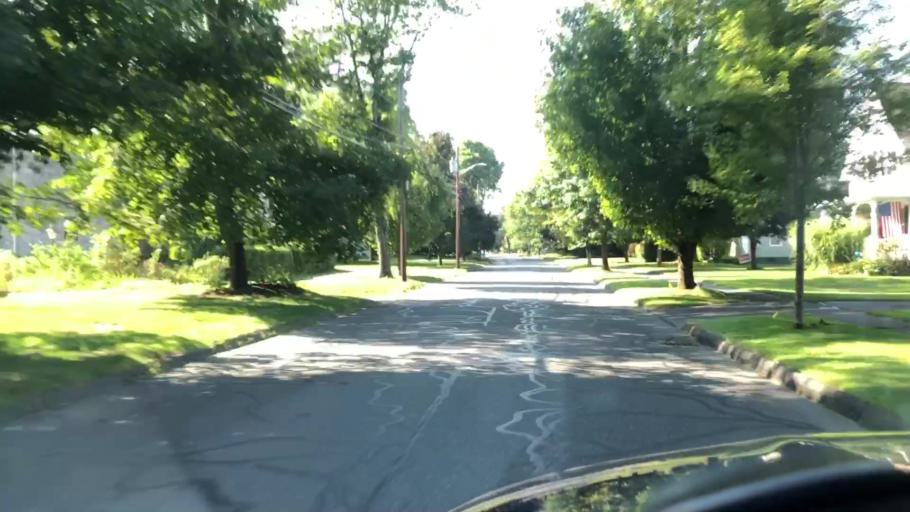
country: US
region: Massachusetts
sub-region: Hampshire County
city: Northampton
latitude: 42.3417
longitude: -72.6718
